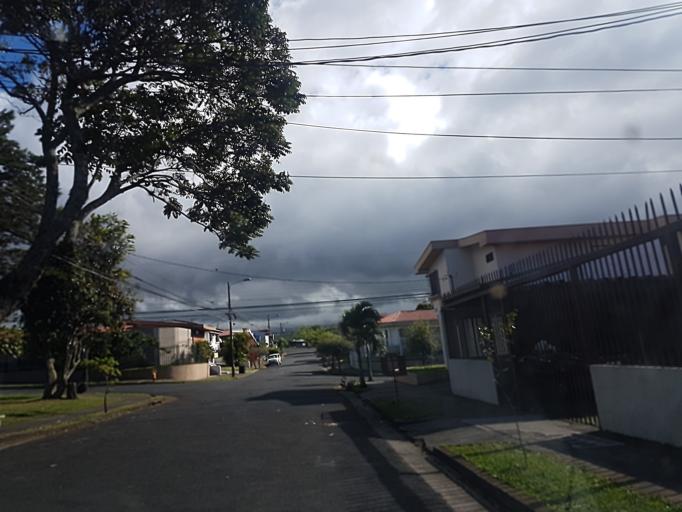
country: CR
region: San Jose
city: San Pedro
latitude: 9.9241
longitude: -84.0640
